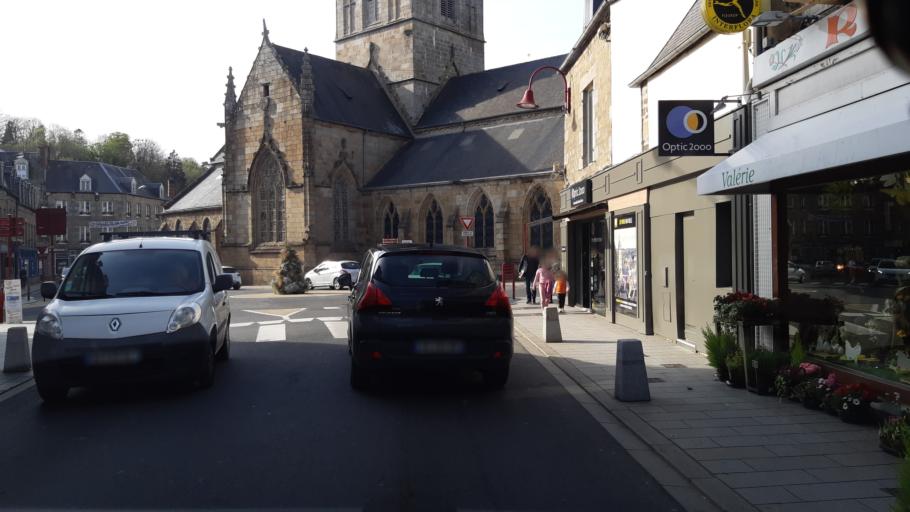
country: FR
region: Lower Normandy
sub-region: Departement de la Manche
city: Villedieu-les-Poeles
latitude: 48.8375
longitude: -1.2223
